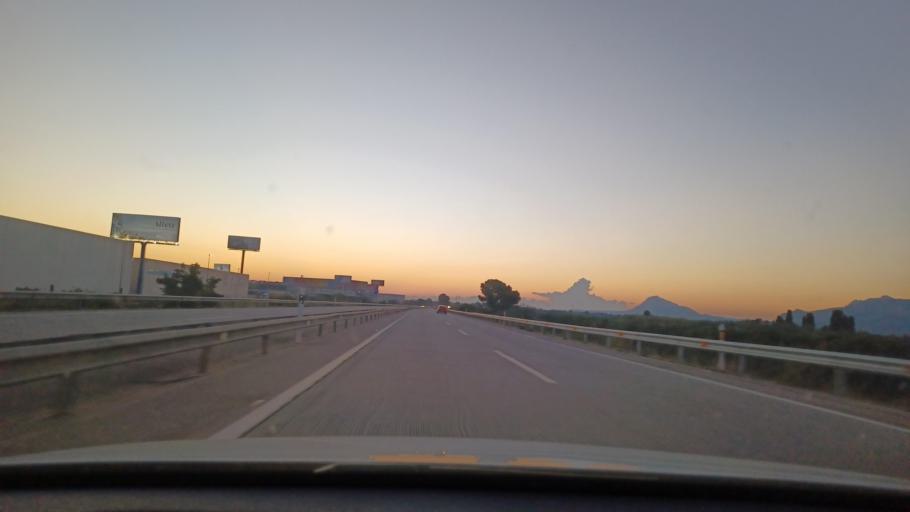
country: ES
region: Valencia
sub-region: Provincia de Valencia
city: Oliva
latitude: 38.8972
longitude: -0.0905
